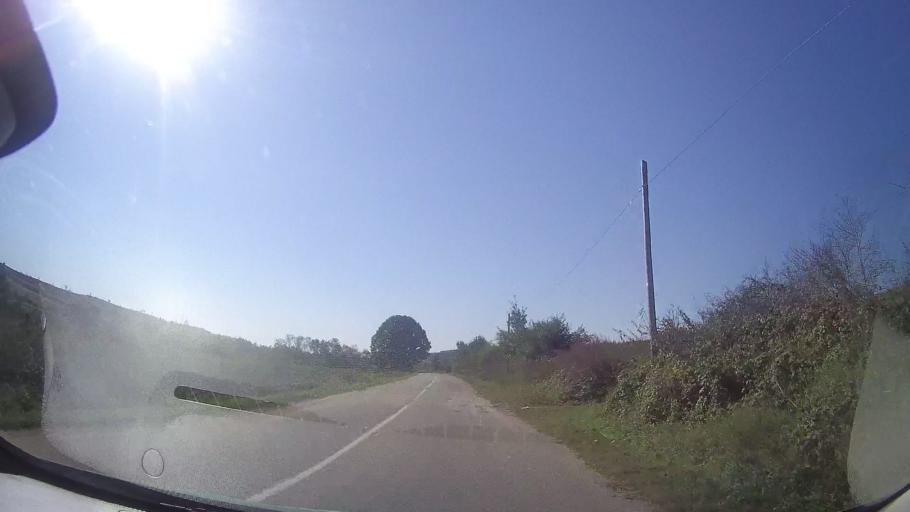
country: RO
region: Timis
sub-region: Comuna Ohaba Lunga
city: Ohaba Lunga
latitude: 45.9020
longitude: 21.9784
